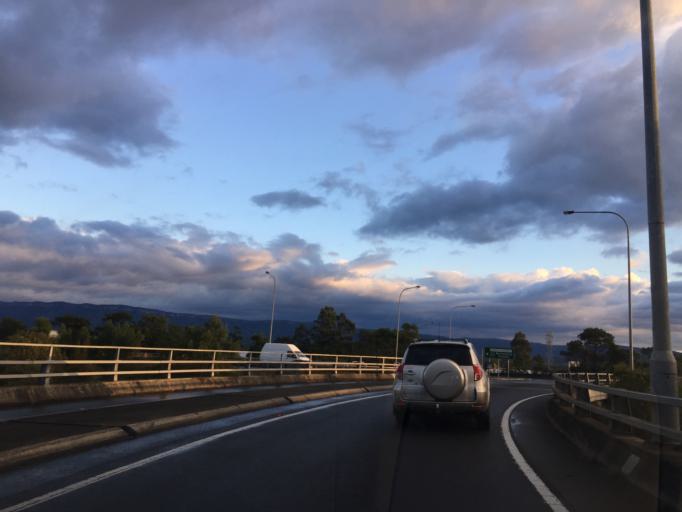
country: AU
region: New South Wales
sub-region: Shellharbour
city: Albion Park Rail
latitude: -34.5740
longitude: 150.8215
